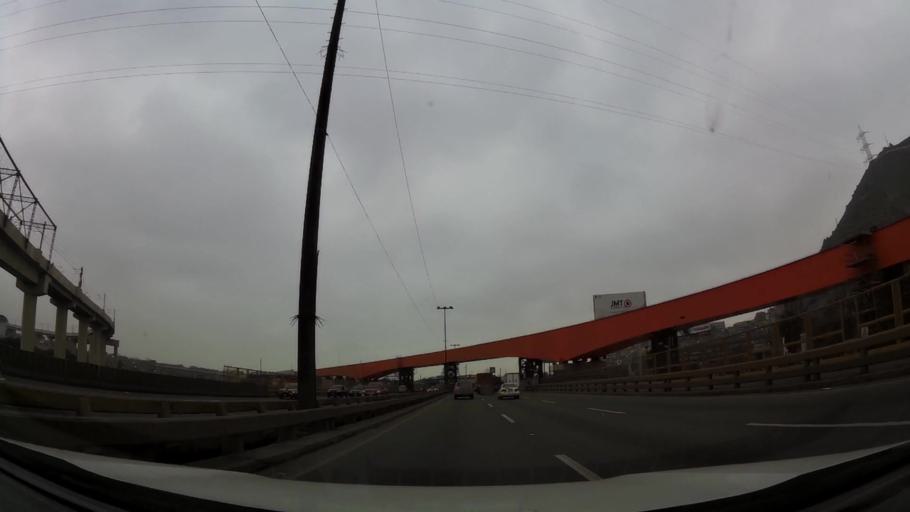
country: PE
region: Lima
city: Lima
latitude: -12.0375
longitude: -77.0131
